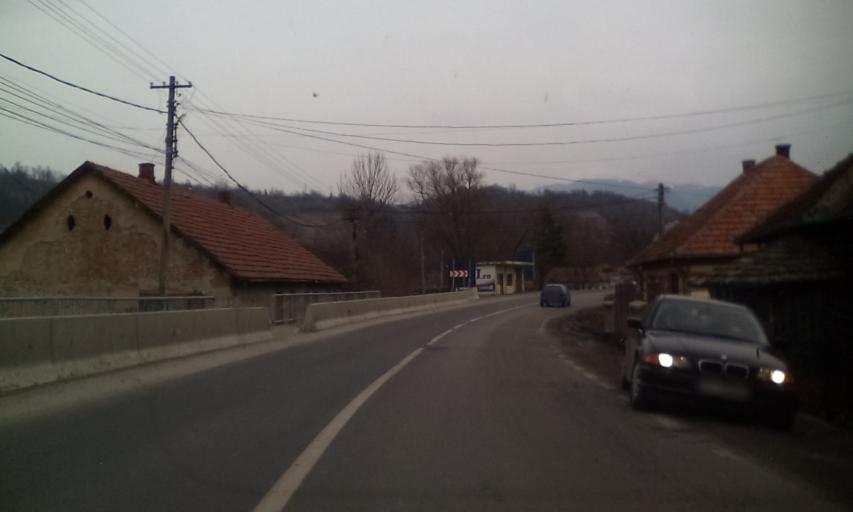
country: RO
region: Hunedoara
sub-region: Comuna Aninoasa
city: Iscroni
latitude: 45.3769
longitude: 23.3379
